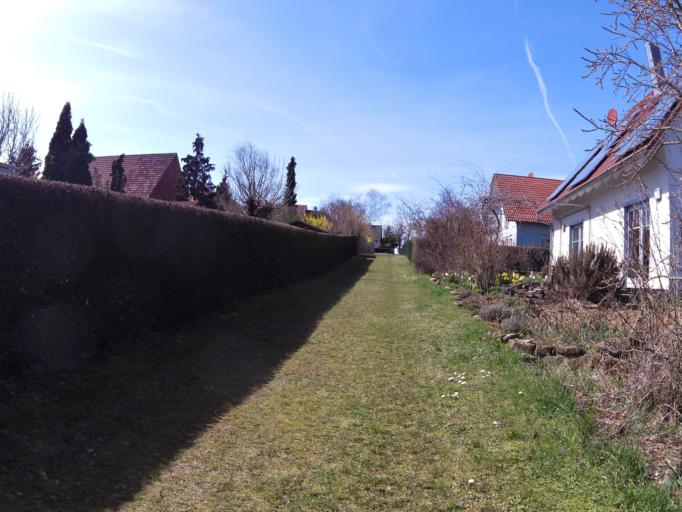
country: DE
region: Bavaria
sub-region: Regierungsbezirk Unterfranken
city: Biebelried
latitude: 49.7996
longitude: 10.1075
